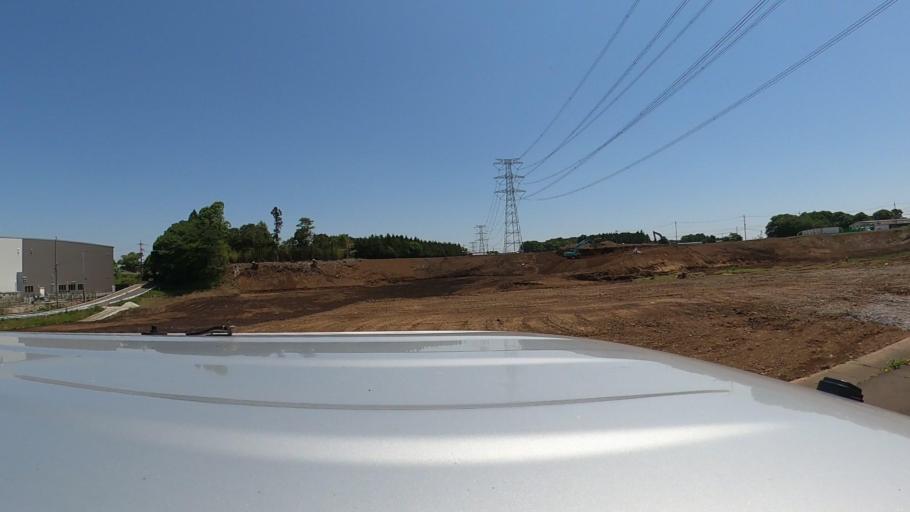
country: JP
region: Ibaraki
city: Ushiku
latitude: 36.0171
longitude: 140.0836
